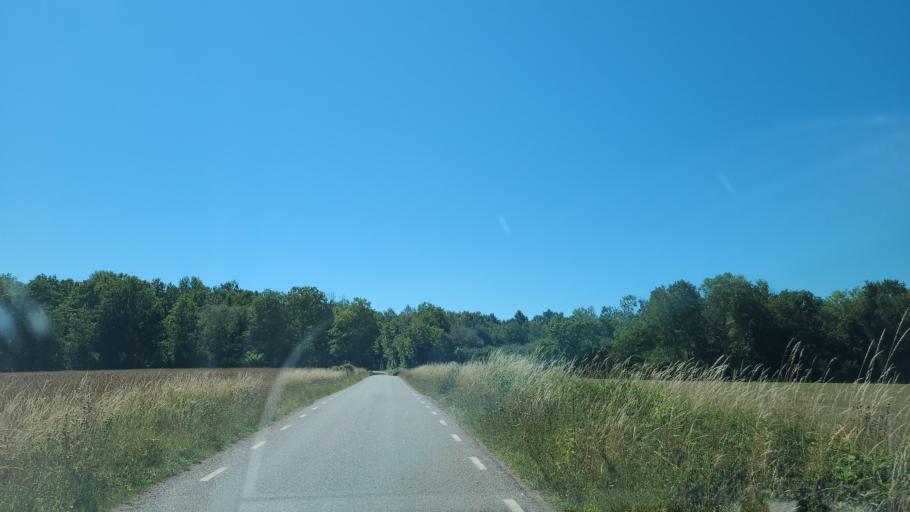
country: SE
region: Kalmar
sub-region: Borgholms Kommun
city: Borgholm
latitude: 56.7569
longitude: 16.6589
